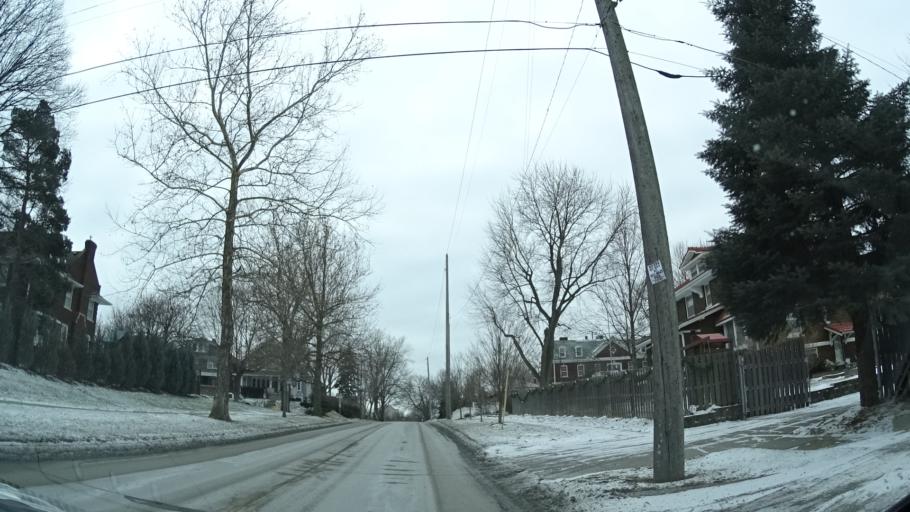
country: US
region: Nebraska
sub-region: Douglas County
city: Omaha
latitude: 41.2621
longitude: -95.9951
